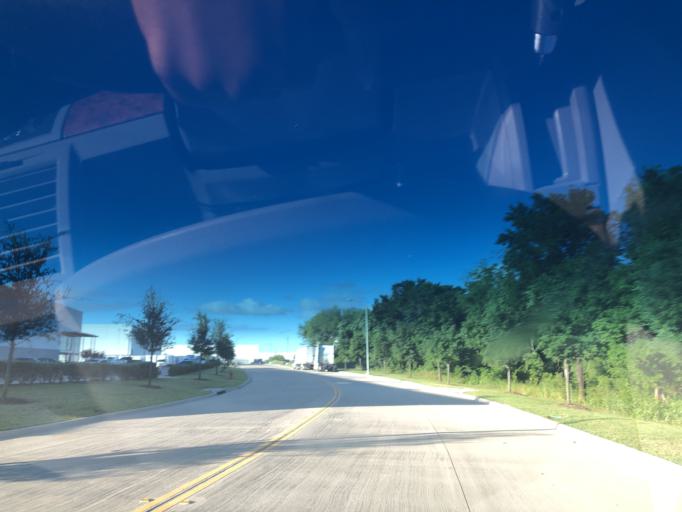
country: US
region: Texas
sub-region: Dallas County
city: Grand Prairie
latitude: 32.7754
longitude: -96.9996
